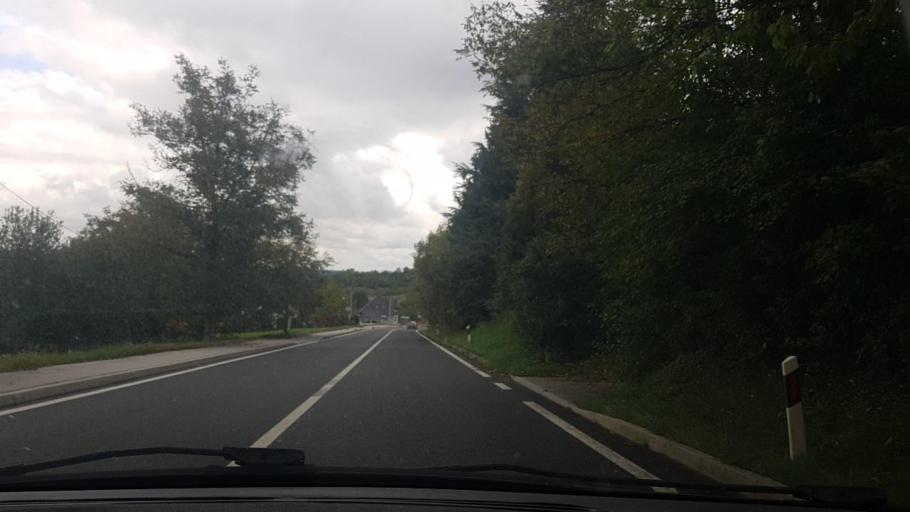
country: SI
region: Bistrica ob Sotli
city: Bistrica ob Sotli
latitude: 46.0649
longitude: 15.7549
